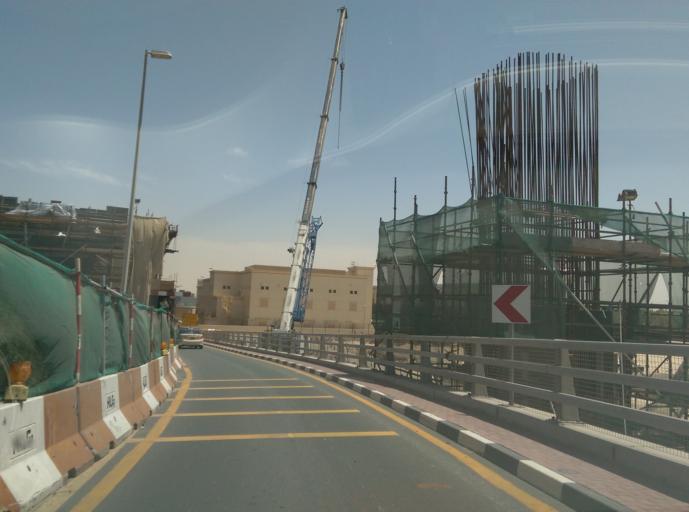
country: AE
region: Dubai
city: Dubai
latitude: 25.0695
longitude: 55.1268
